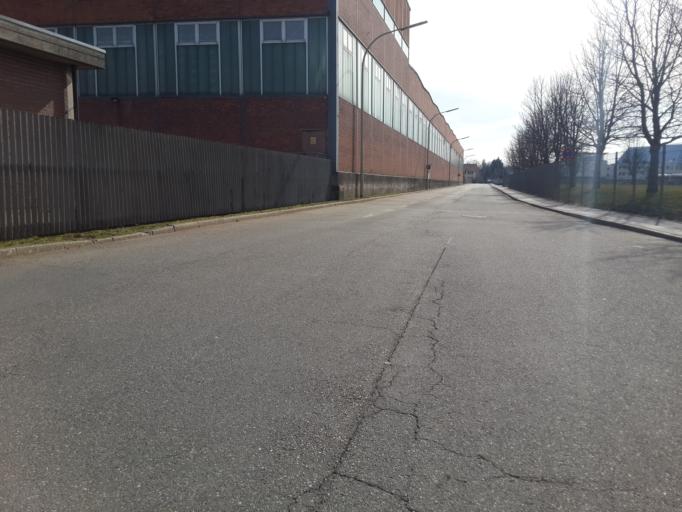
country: DE
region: Baden-Wuerttemberg
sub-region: Regierungsbezirk Stuttgart
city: Neckarsulm
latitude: 49.1692
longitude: 9.2147
